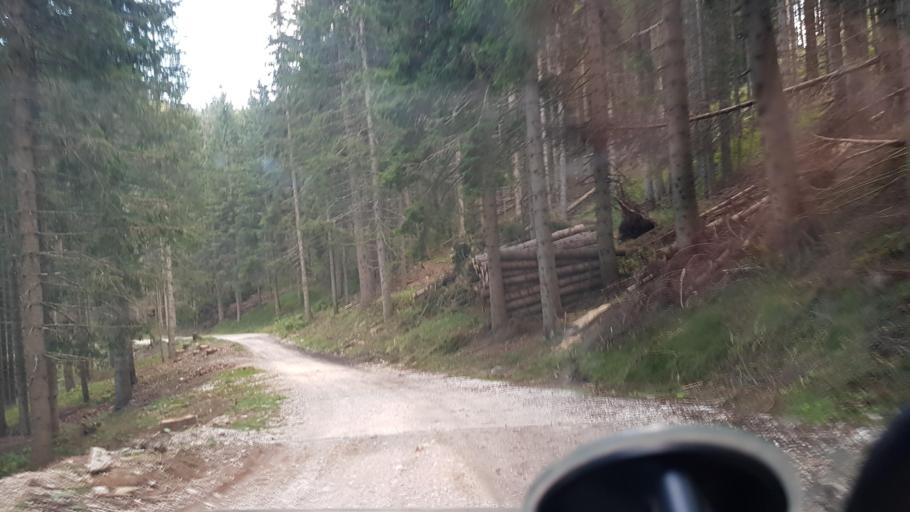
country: IT
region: Veneto
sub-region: Provincia di Belluno
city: San Pietro di Cadore
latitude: 46.6047
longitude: 12.5925
